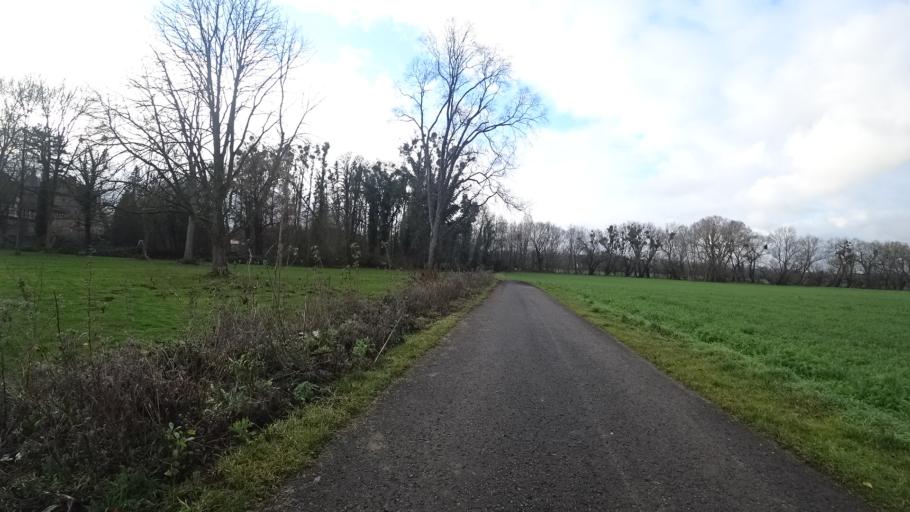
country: DE
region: Lower Saxony
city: Lauenau
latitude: 52.2762
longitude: 9.3670
